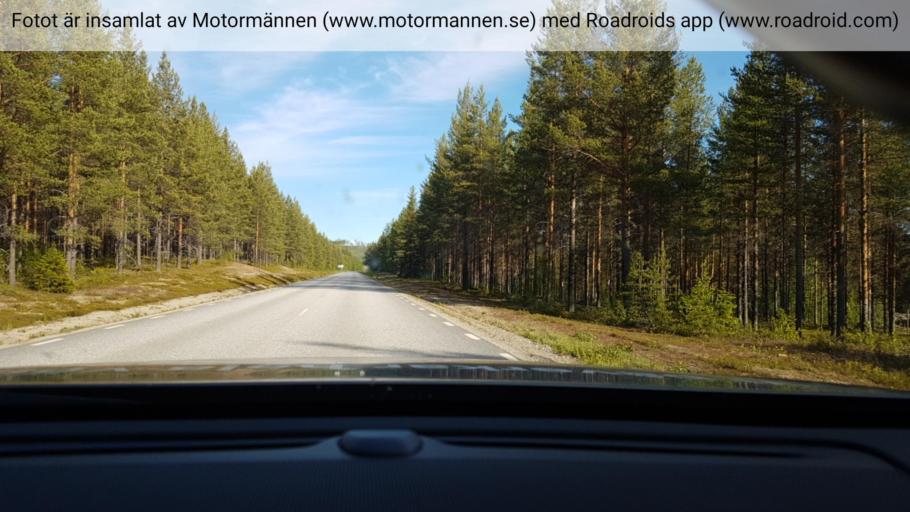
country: SE
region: Vaesterbotten
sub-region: Vindelns Kommun
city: Vindeln
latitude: 64.3648
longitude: 19.4372
